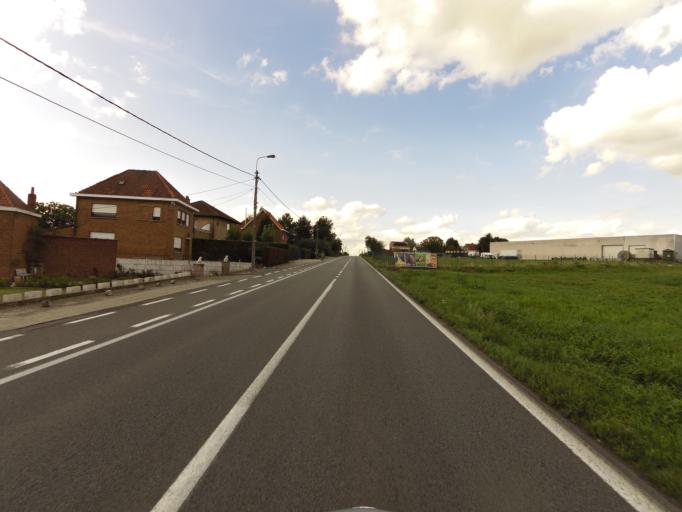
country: BE
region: Flanders
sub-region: Provincie West-Vlaanderen
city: Waregem
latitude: 50.8642
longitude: 3.4463
